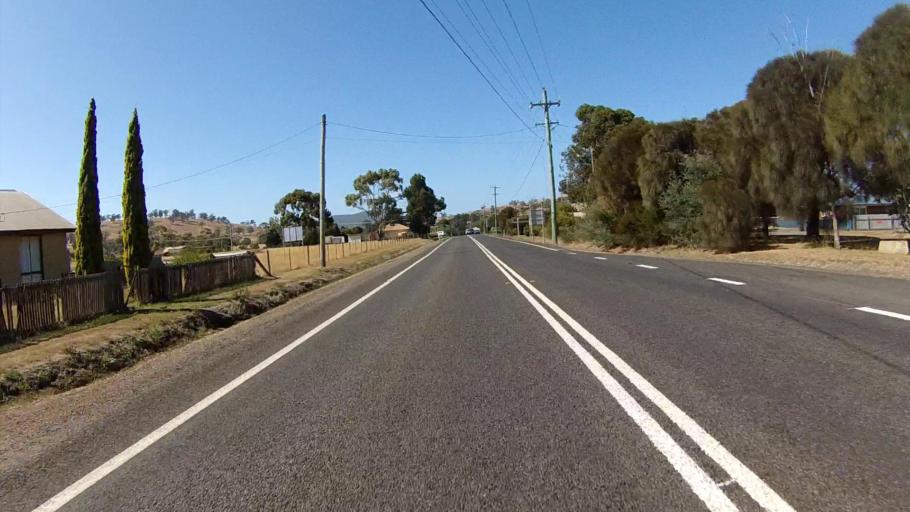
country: AU
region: Tasmania
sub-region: Sorell
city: Sorell
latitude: -42.5016
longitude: 147.9153
